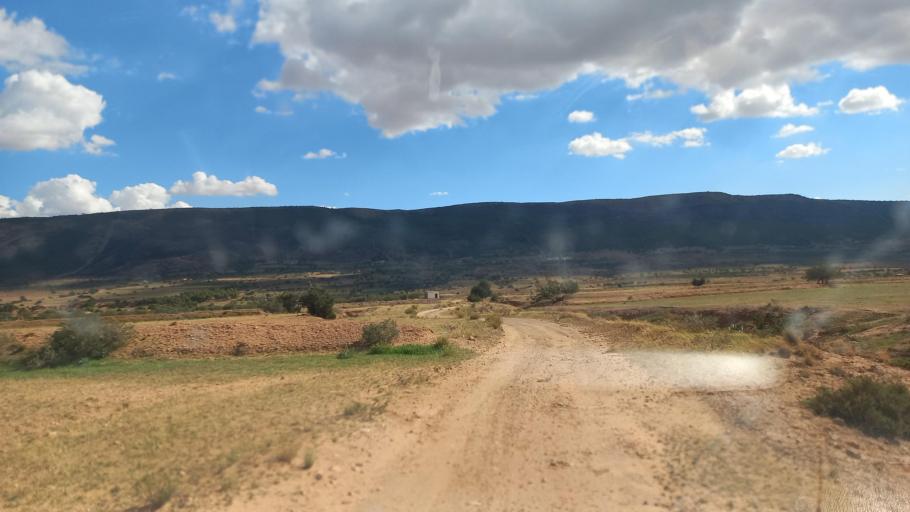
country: TN
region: Al Qasrayn
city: Kasserine
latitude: 35.3719
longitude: 8.8845
